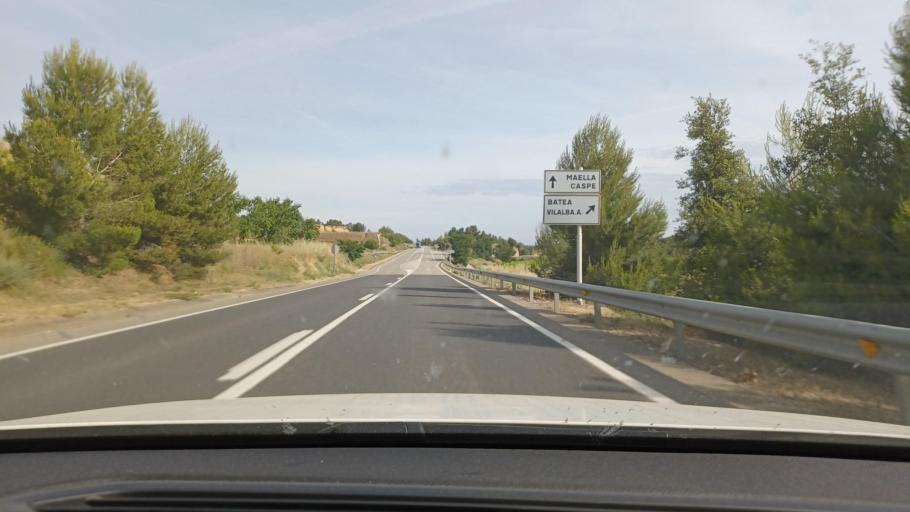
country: ES
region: Catalonia
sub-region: Provincia de Tarragona
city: Batea
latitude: 41.0755
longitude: 0.3299
